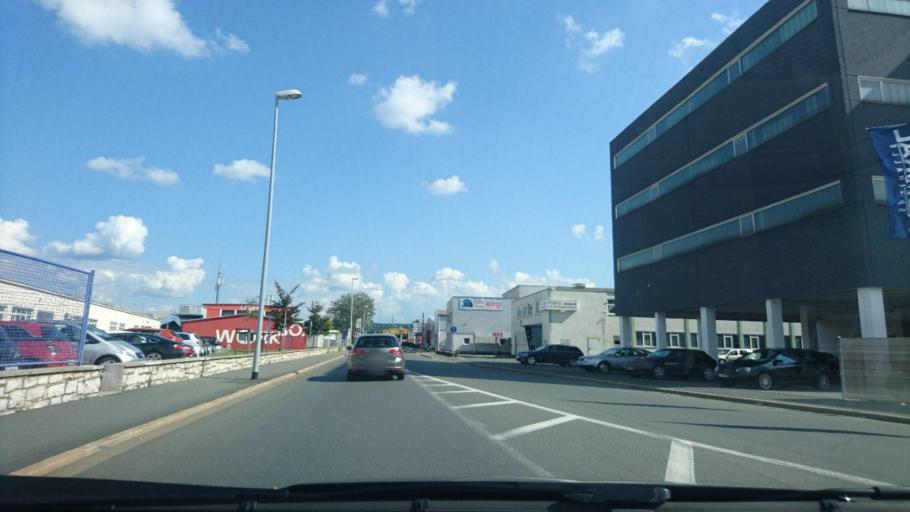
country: DE
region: Bavaria
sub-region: Upper Franconia
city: Bayreuth
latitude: 49.9588
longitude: 11.5993
